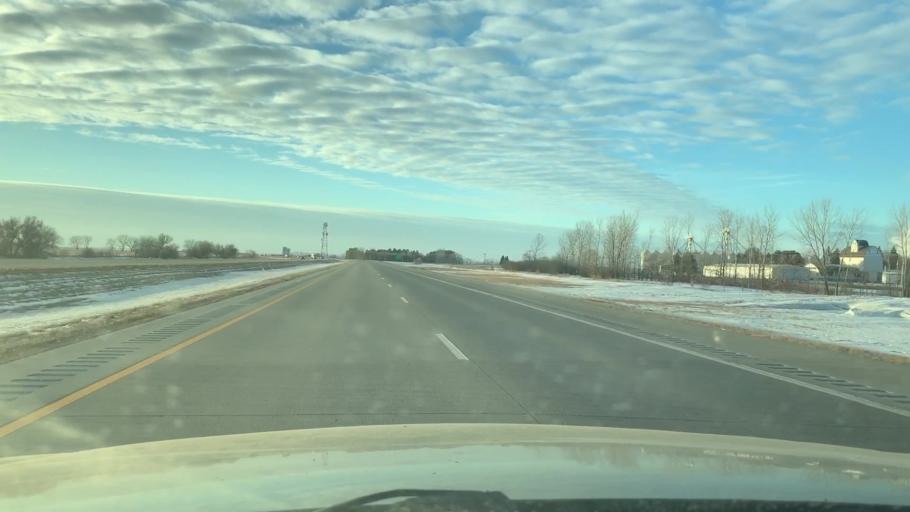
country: US
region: North Dakota
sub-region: Cass County
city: Casselton
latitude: 46.8749
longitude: -97.2302
